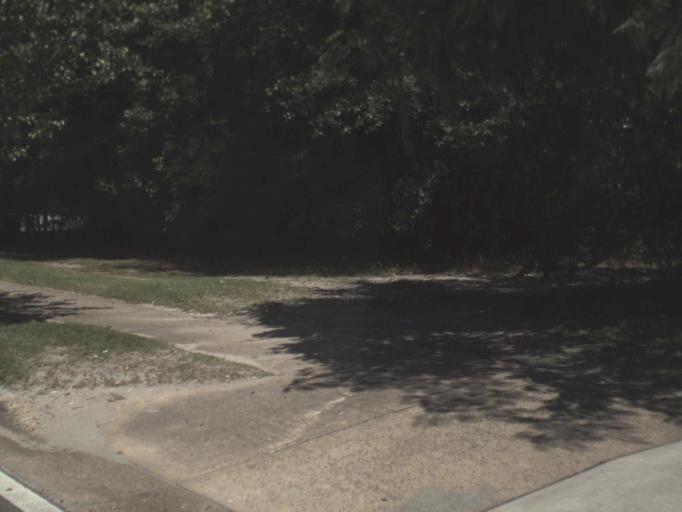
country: US
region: Florida
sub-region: Baker County
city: Macclenny
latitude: 30.2819
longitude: -82.1250
